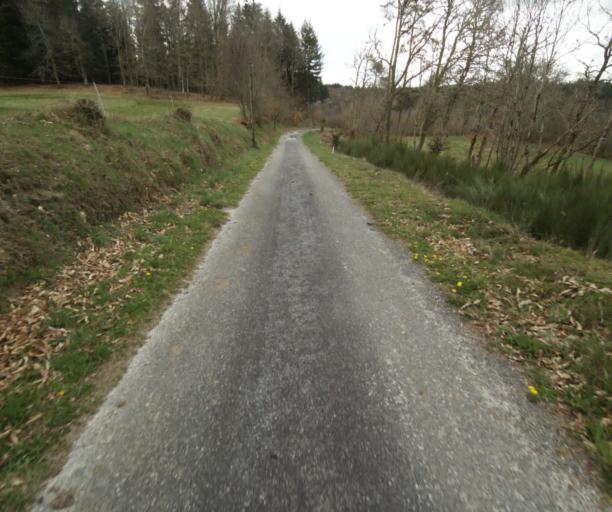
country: FR
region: Limousin
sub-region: Departement de la Correze
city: Correze
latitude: 45.2672
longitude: 1.9576
